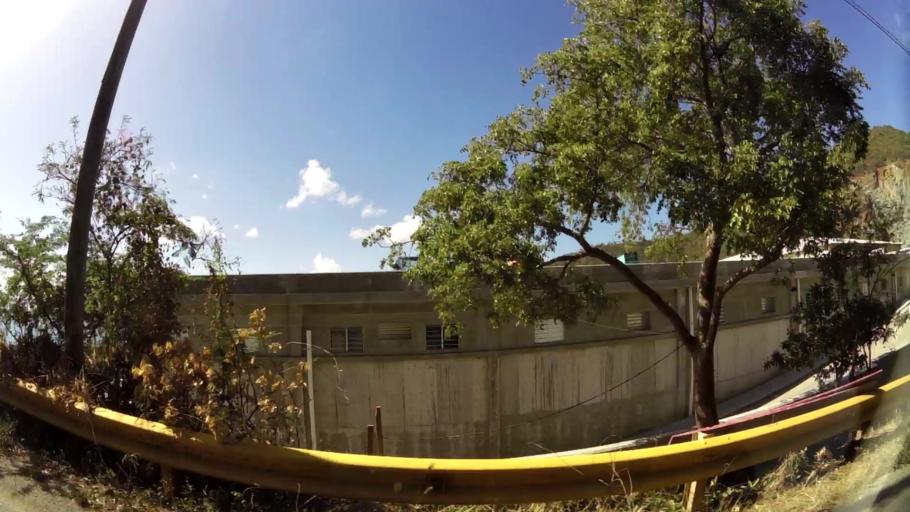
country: VG
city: Tortola
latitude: 18.4176
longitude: -64.5978
